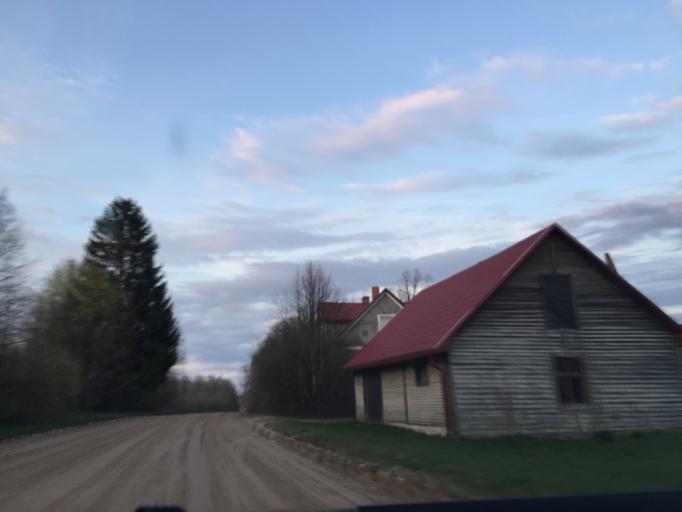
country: LV
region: Aluksnes Rajons
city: Aluksne
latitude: 57.3532
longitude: 26.9796
